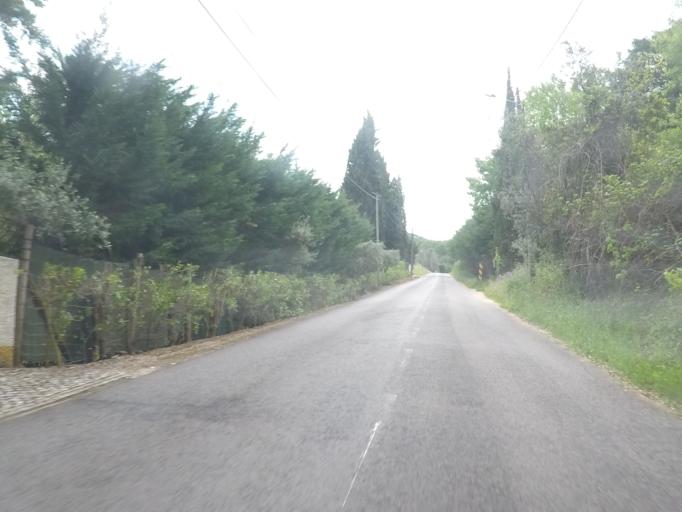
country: PT
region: Setubal
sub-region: Palmela
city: Quinta do Anjo
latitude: 38.5026
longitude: -8.9845
